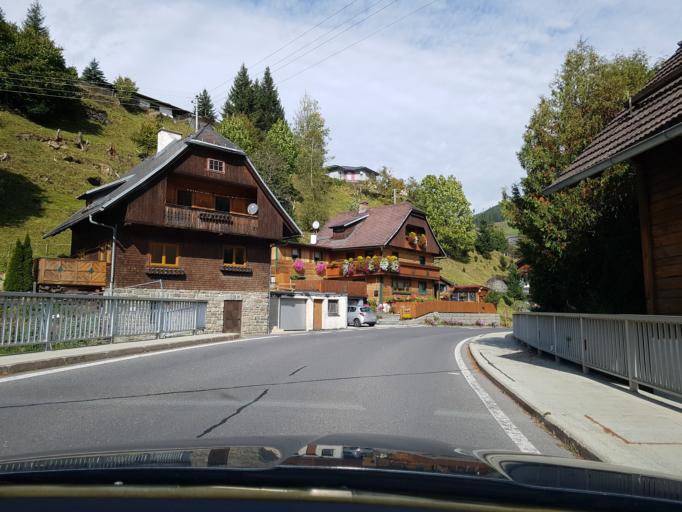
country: AT
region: Carinthia
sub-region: Politischer Bezirk Spittal an der Drau
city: Kleinkirchheim
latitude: 46.8562
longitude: 13.8915
